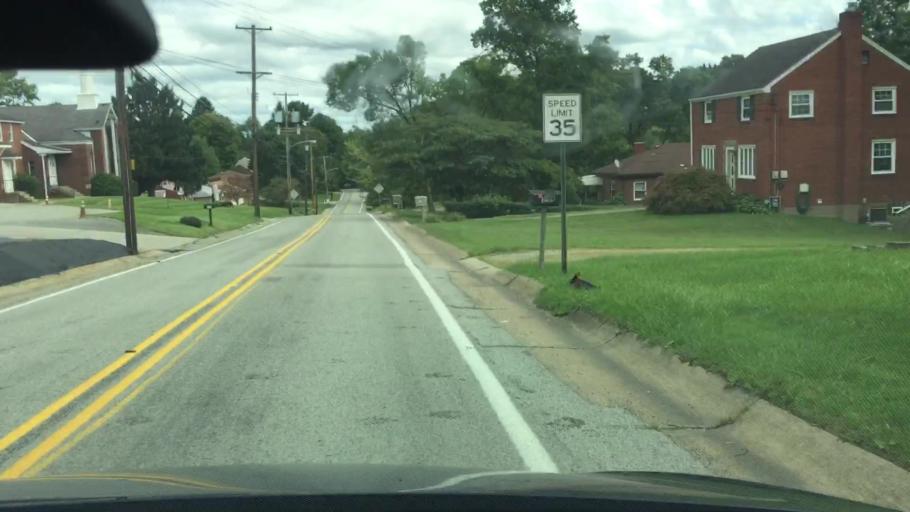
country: US
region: Pennsylvania
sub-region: Allegheny County
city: Penn Hills
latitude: 40.4896
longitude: -79.8196
